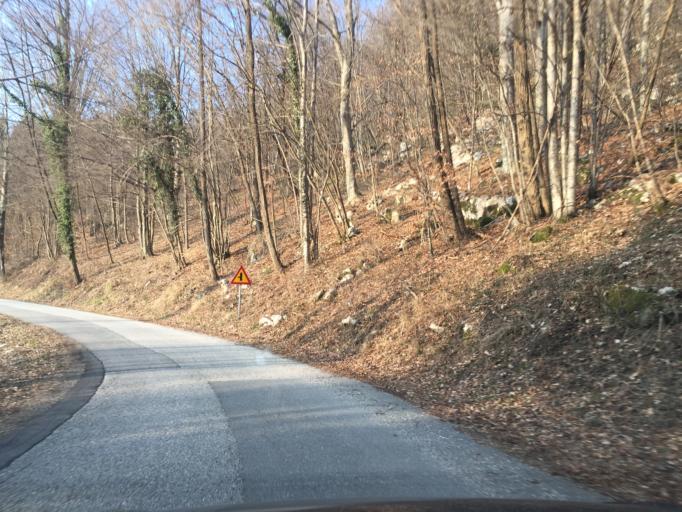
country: SI
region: Kanal
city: Kanal
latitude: 46.0522
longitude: 13.6692
